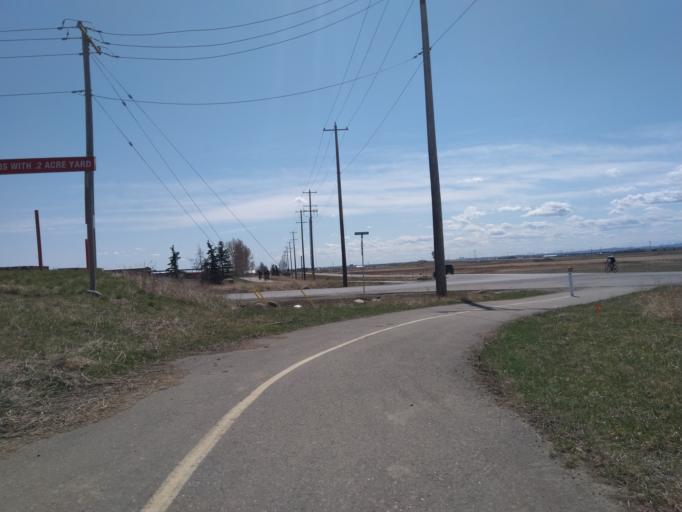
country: CA
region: Alberta
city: Chestermere
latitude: 50.9707
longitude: -113.9115
